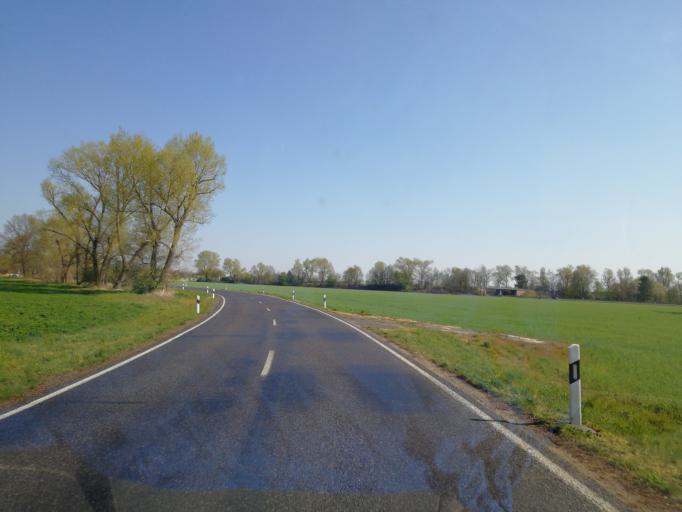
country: DE
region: Brandenburg
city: Calau
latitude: 51.7551
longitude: 13.8591
